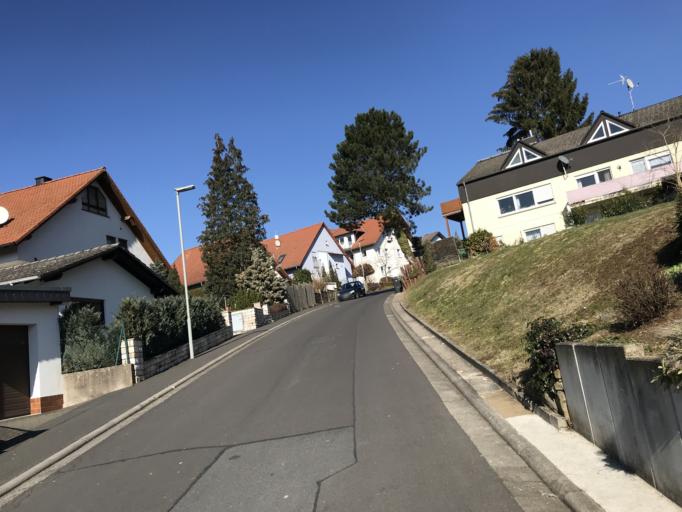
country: DE
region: Hesse
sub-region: Regierungsbezirk Darmstadt
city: Nidda
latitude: 50.4059
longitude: 9.0139
